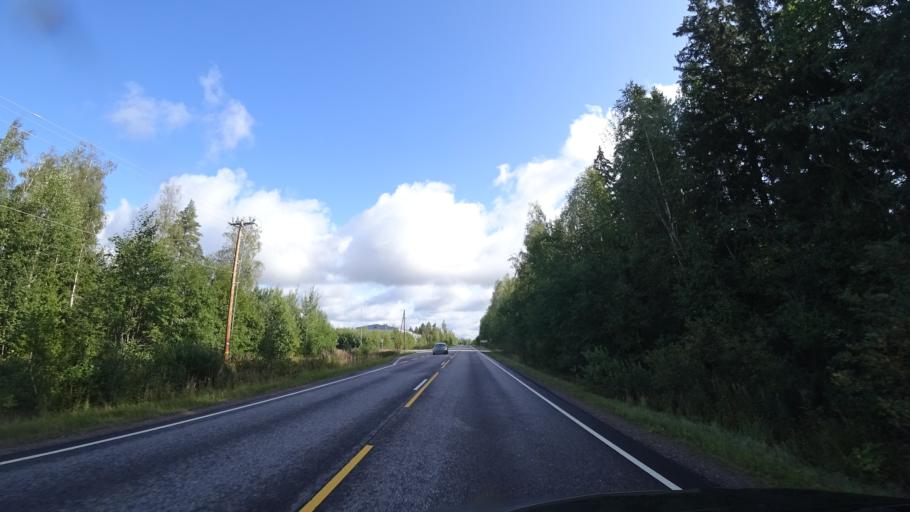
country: FI
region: Uusimaa
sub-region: Helsinki
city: Hyvinge
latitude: 60.5458
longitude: 24.9372
